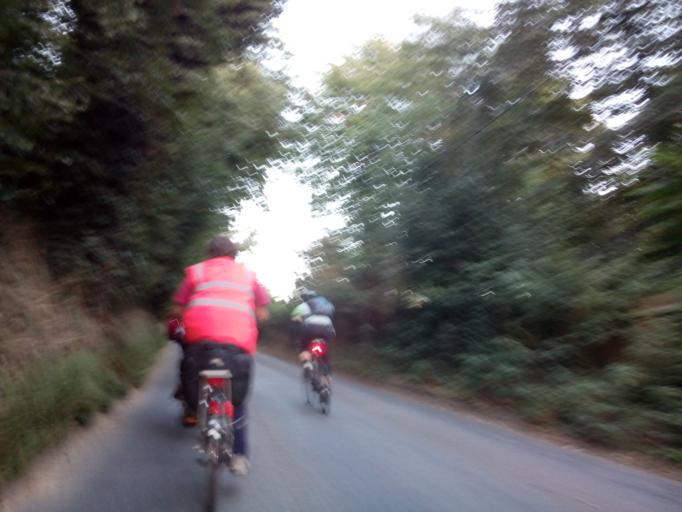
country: GB
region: England
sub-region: Suffolk
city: Kesgrave
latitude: 52.0913
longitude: 1.2403
